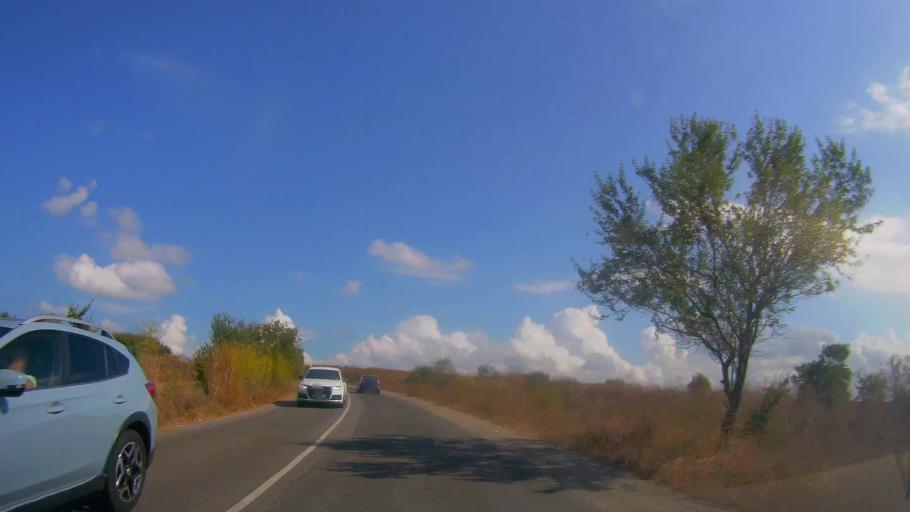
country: BG
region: Burgas
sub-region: Obshtina Burgas
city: Burgas
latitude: 42.4774
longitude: 27.3904
